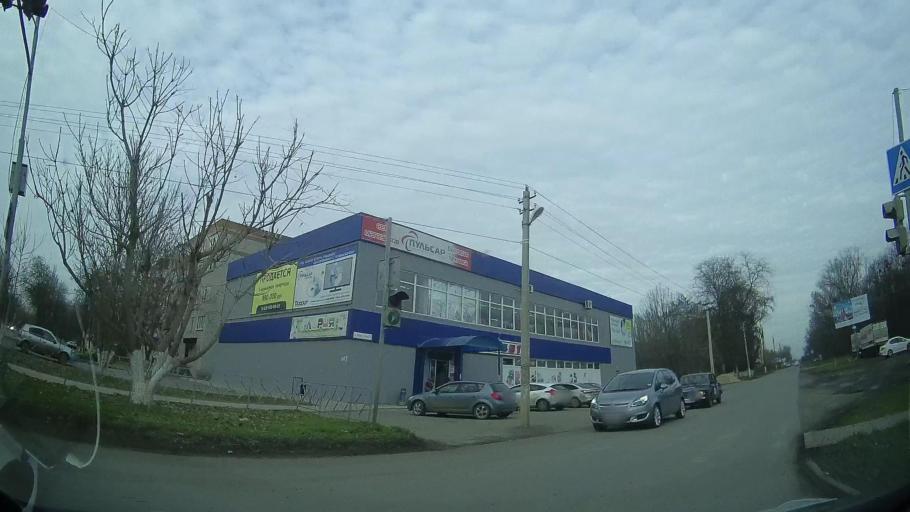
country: RU
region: Rostov
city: Zernograd
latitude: 46.8534
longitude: 40.3129
